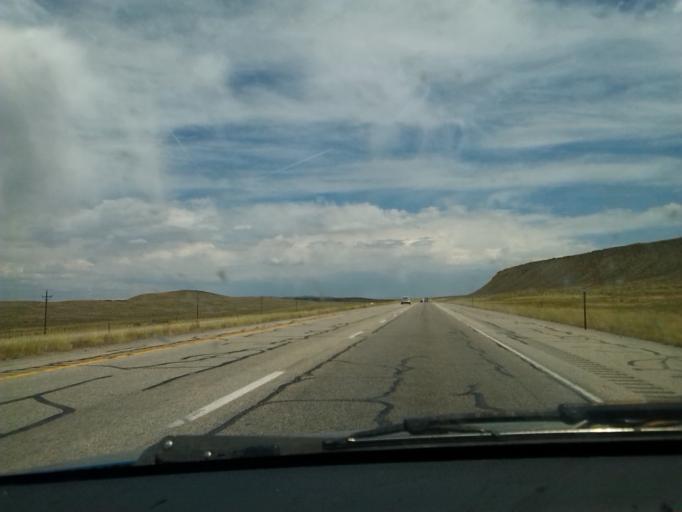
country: US
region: Wyoming
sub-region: Carbon County
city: Saratoga
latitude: 41.7439
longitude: -106.9080
